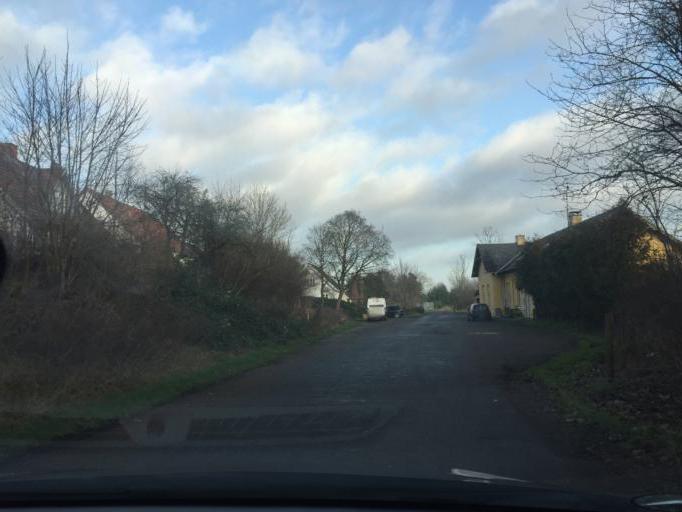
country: DK
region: South Denmark
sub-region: Faaborg-Midtfyn Kommune
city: Ringe
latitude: 55.1925
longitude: 10.3487
